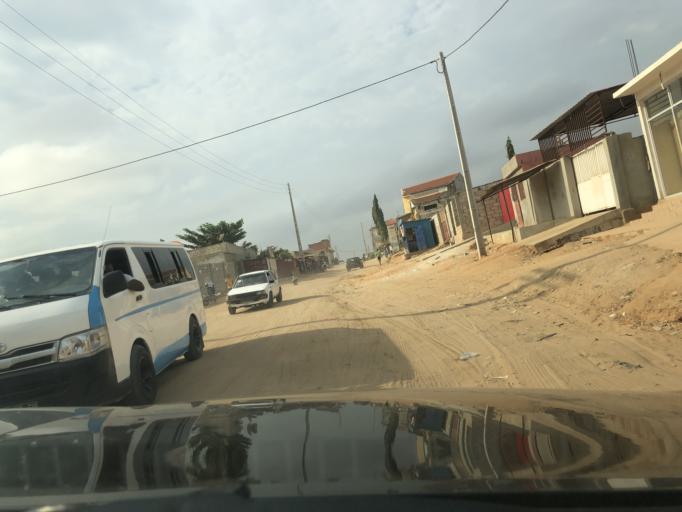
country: AO
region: Luanda
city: Luanda
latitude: -8.9293
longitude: 13.2308
